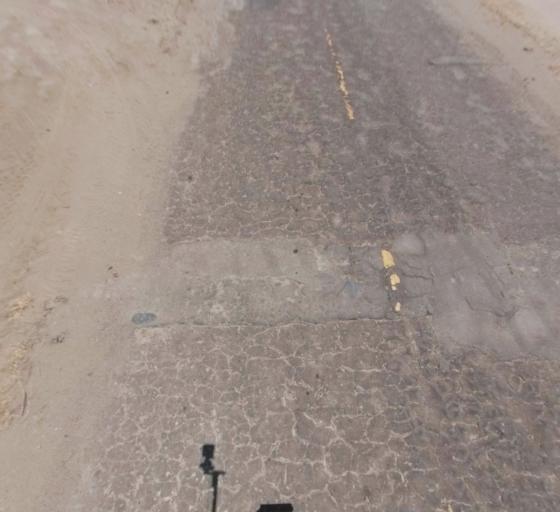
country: US
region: California
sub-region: Madera County
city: Parkwood
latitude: 36.8731
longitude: -120.0787
